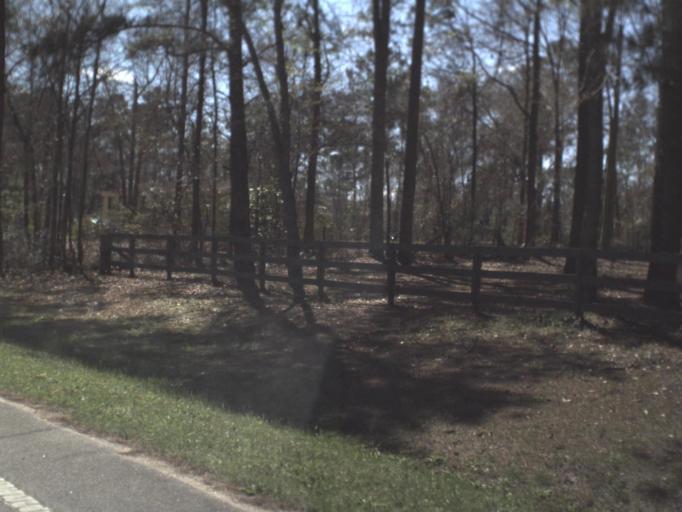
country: US
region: Florida
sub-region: Gadsden County
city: Quincy
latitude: 30.6207
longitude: -84.5941
